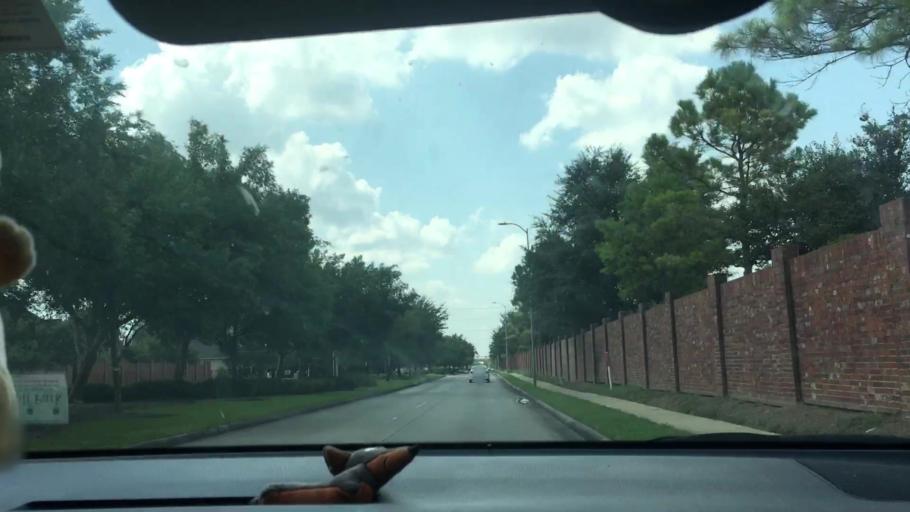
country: US
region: Texas
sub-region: Harris County
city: Bunker Hill Village
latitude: 29.7236
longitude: -95.5717
